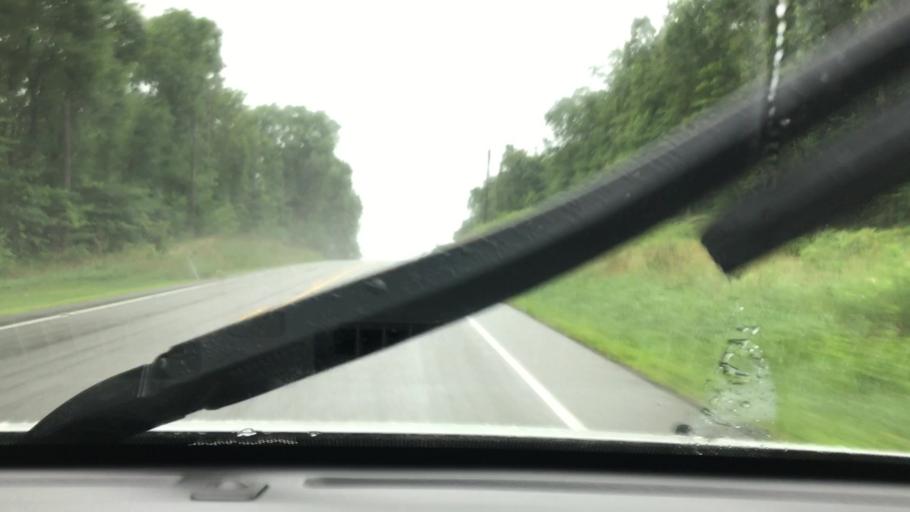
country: US
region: Pennsylvania
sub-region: Centre County
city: Philipsburg
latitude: 40.8498
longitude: -78.2196
